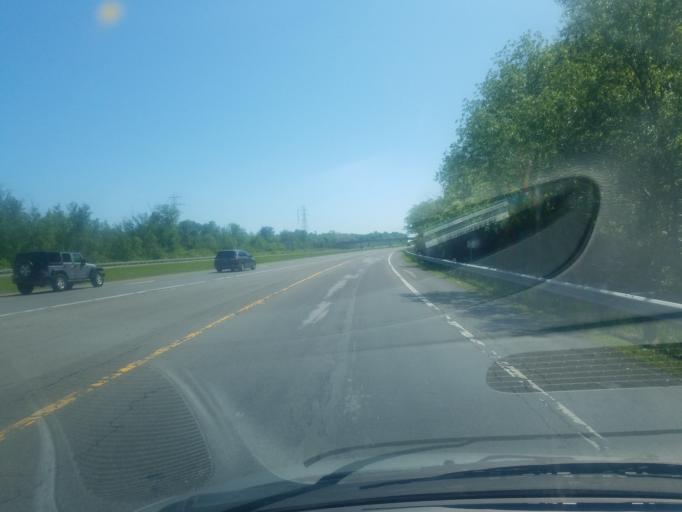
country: US
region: Ohio
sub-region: Erie County
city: Sandusky
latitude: 41.4008
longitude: -82.6515
